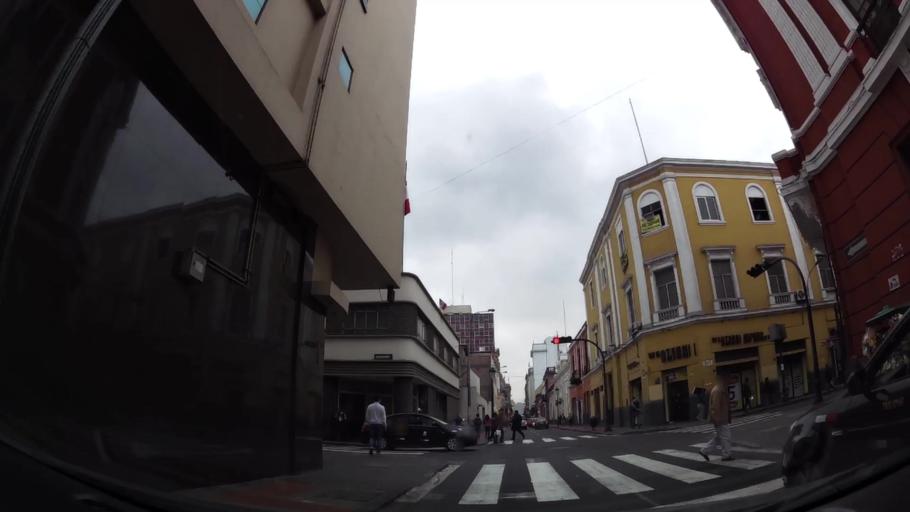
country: PE
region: Lima
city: Lima
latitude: -12.0506
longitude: -77.0332
